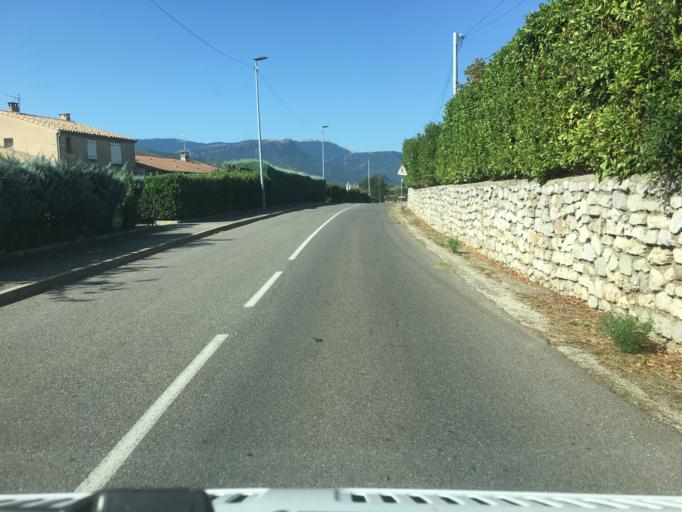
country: FR
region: Provence-Alpes-Cote d'Azur
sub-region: Departement des Alpes-de-Haute-Provence
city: Sisteron
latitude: 44.1831
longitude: 5.9347
